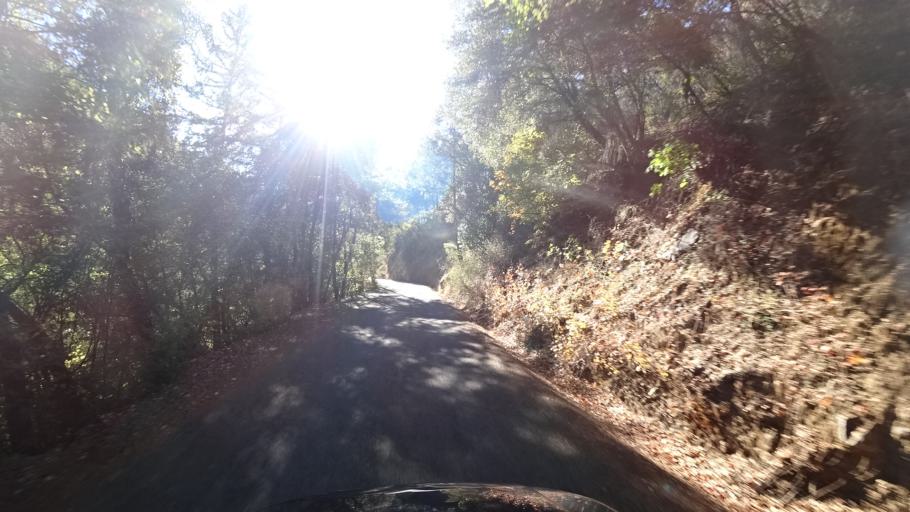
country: US
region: California
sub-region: Humboldt County
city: Willow Creek
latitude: 41.2782
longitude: -123.2745
